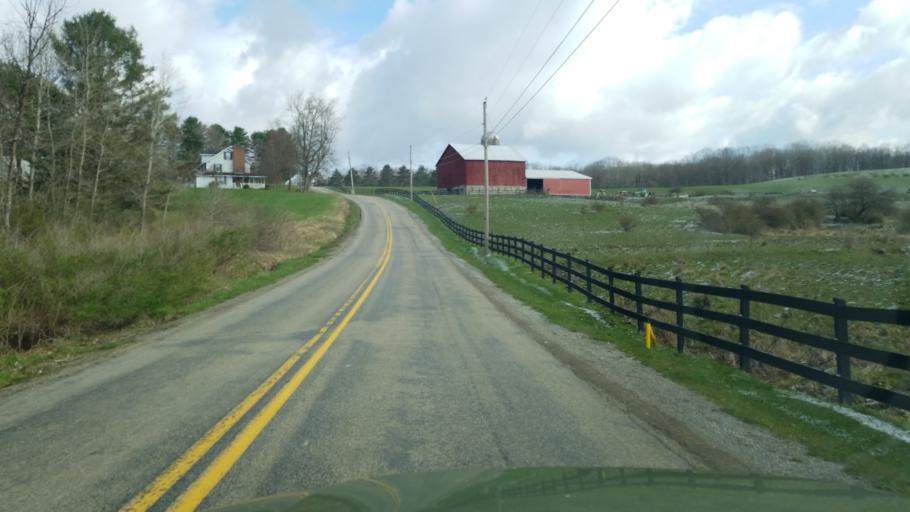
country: US
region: Pennsylvania
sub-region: Jefferson County
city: Brockway
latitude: 41.2660
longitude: -78.8416
